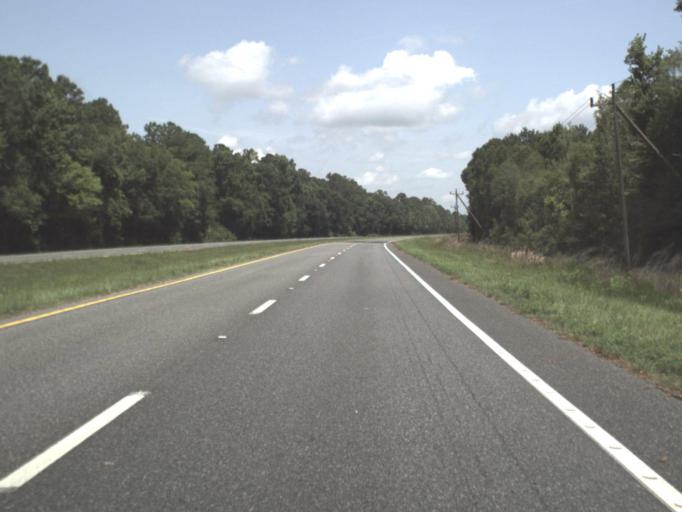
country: US
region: Florida
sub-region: Taylor County
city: Perry
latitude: 29.9292
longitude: -83.4429
